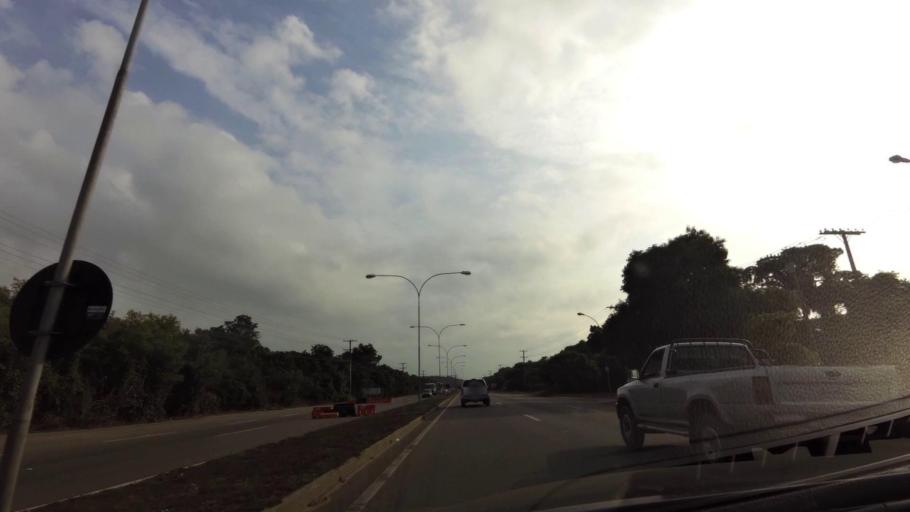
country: BR
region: Espirito Santo
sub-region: Vila Velha
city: Vila Velha
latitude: -20.4102
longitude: -40.3272
